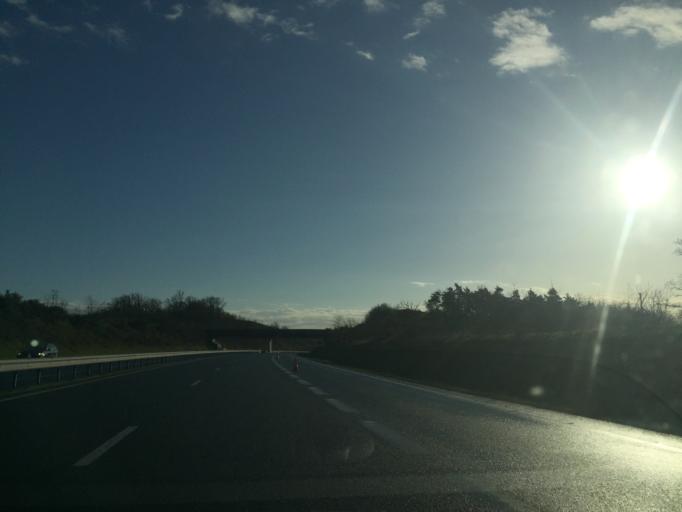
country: FR
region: Limousin
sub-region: Departement de la Correze
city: Cublac
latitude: 45.1732
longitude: 1.3156
